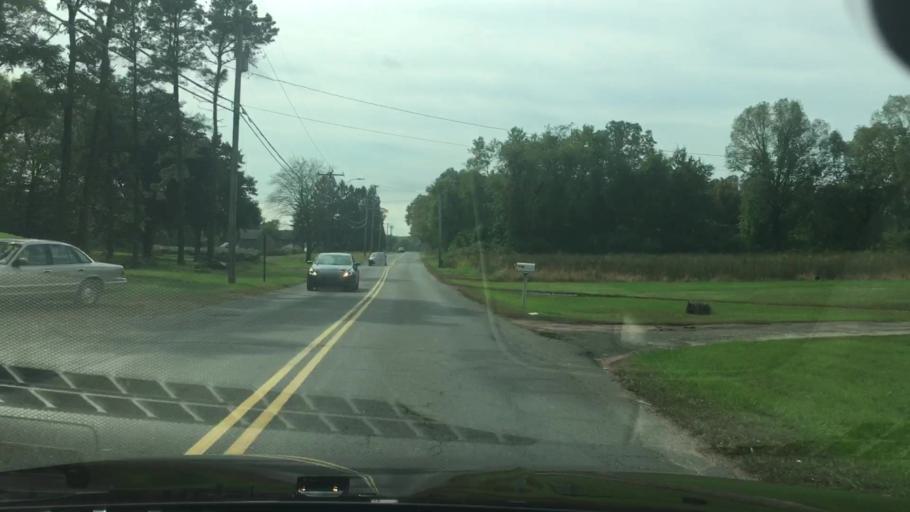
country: US
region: Connecticut
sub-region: Hartford County
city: Broad Brook
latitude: 41.8874
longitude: -72.5401
